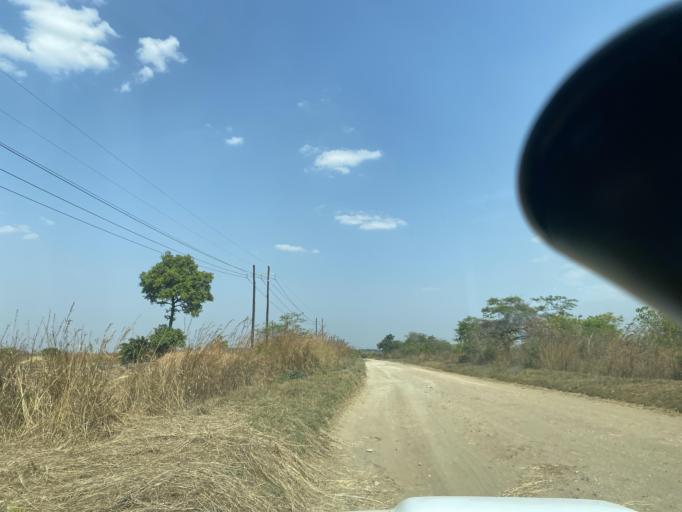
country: ZM
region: Lusaka
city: Lusaka
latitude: -15.3151
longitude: 28.0573
